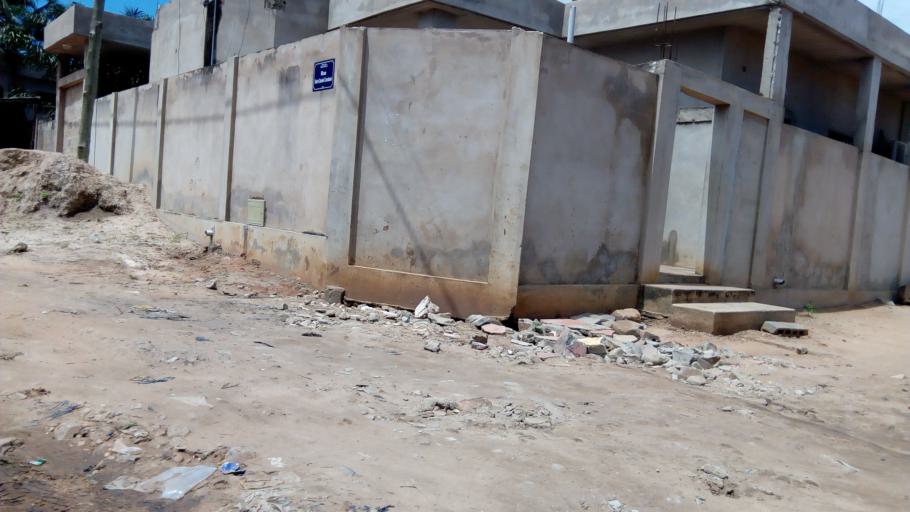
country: TG
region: Maritime
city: Lome
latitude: 6.1713
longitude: 1.1800
